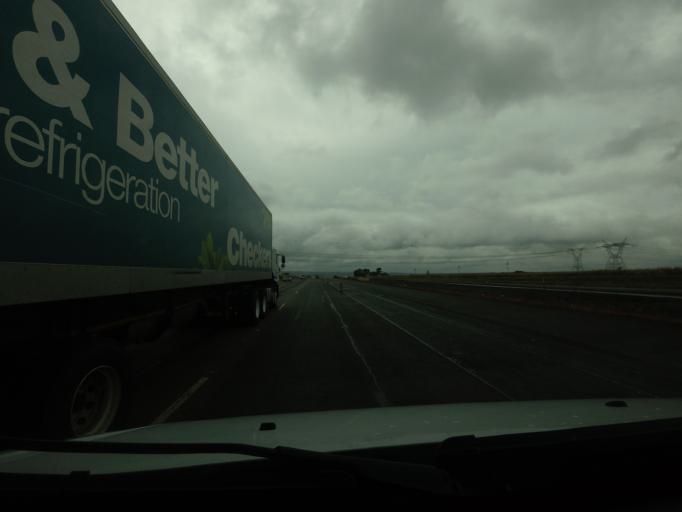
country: ZA
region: Mpumalanga
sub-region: Nkangala District Municipality
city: Witbank
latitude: -25.8742
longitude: 29.1380
